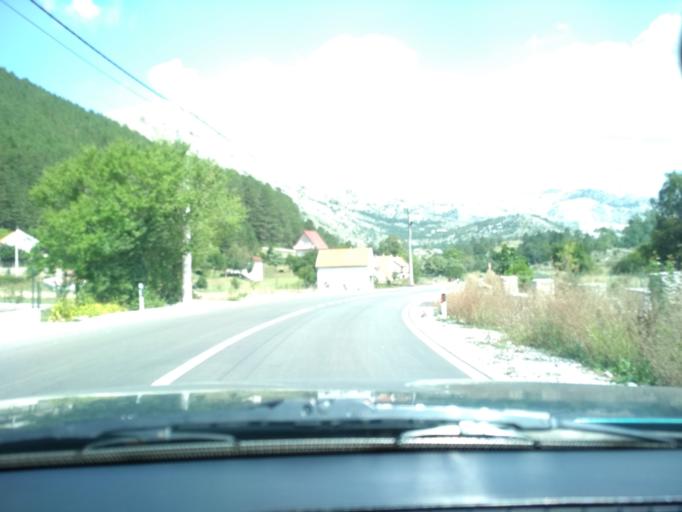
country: ME
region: Kotor
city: Kotor
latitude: 42.4292
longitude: 18.8050
